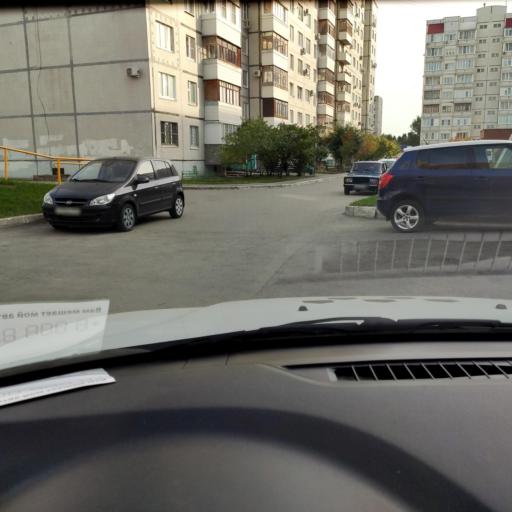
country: RU
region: Samara
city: Tol'yatti
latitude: 53.5326
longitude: 49.3934
